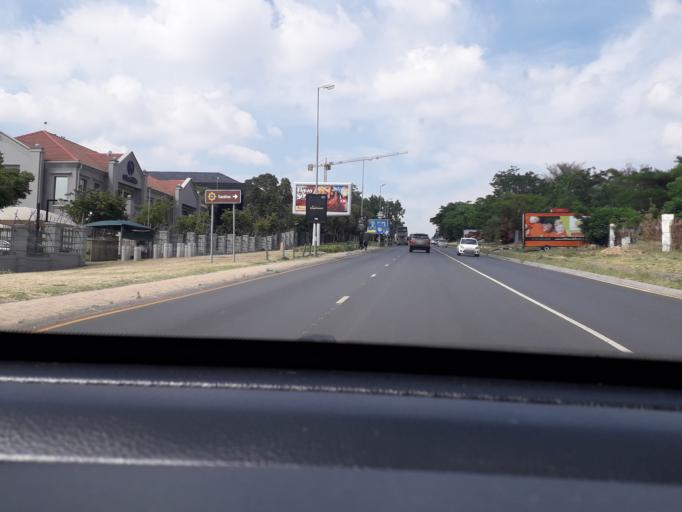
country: ZA
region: Gauteng
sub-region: City of Johannesburg Metropolitan Municipality
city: Modderfontein
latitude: -26.0766
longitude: 28.0645
